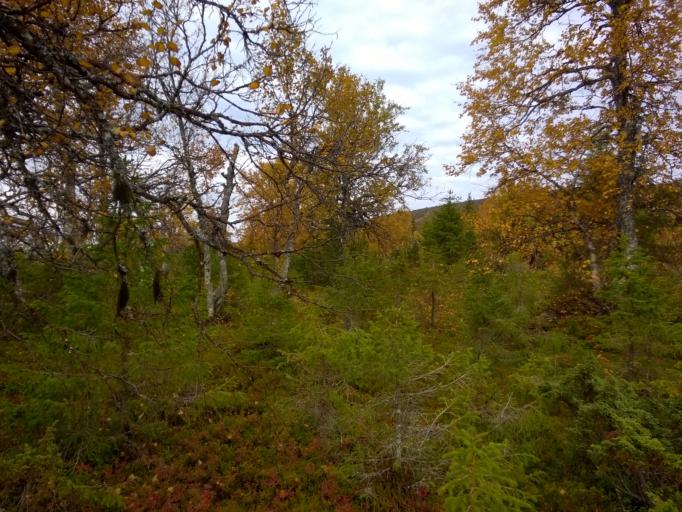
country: FI
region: Lapland
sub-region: Tunturi-Lappi
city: Muonio
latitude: 67.9703
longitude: 24.0960
